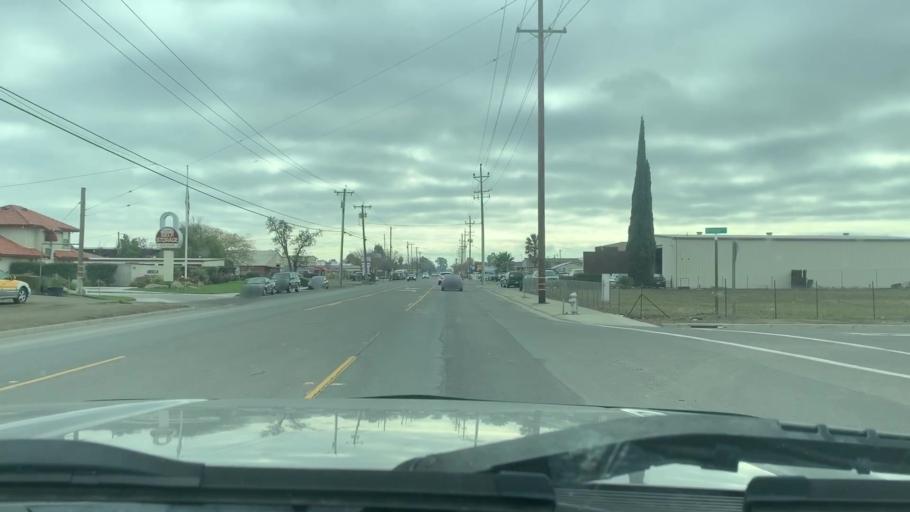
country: US
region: California
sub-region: Merced County
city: Los Banos
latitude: 37.0649
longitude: -120.8353
